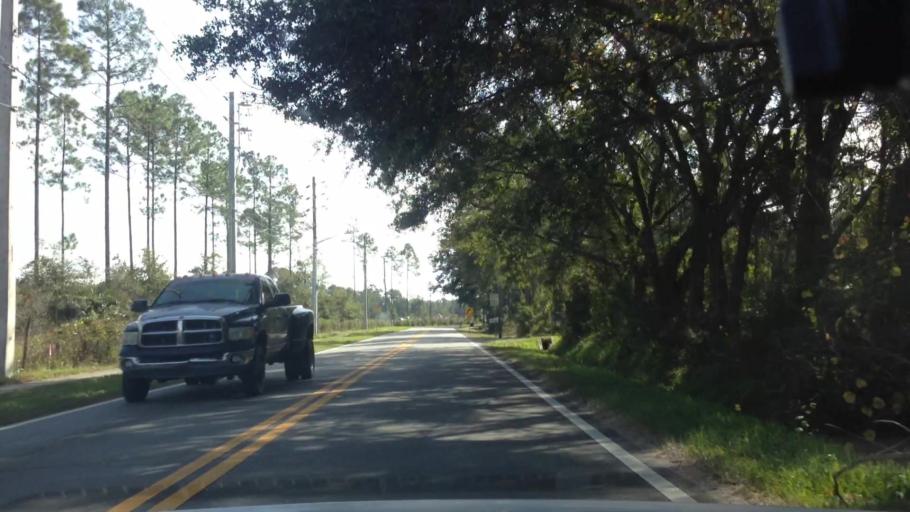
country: US
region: Florida
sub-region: Nassau County
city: Yulee
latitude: 30.5032
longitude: -81.5778
